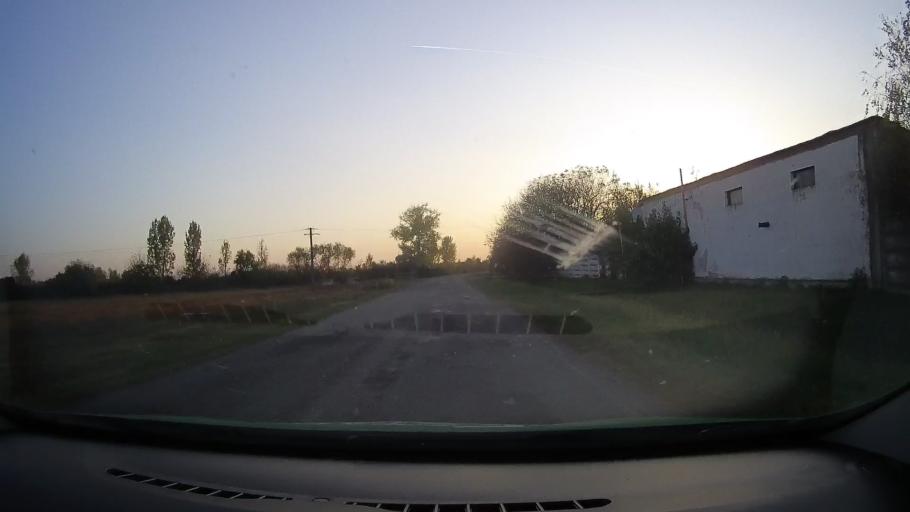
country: RO
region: Arad
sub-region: Comuna Sicula
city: Sicula
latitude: 46.4219
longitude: 21.7462
